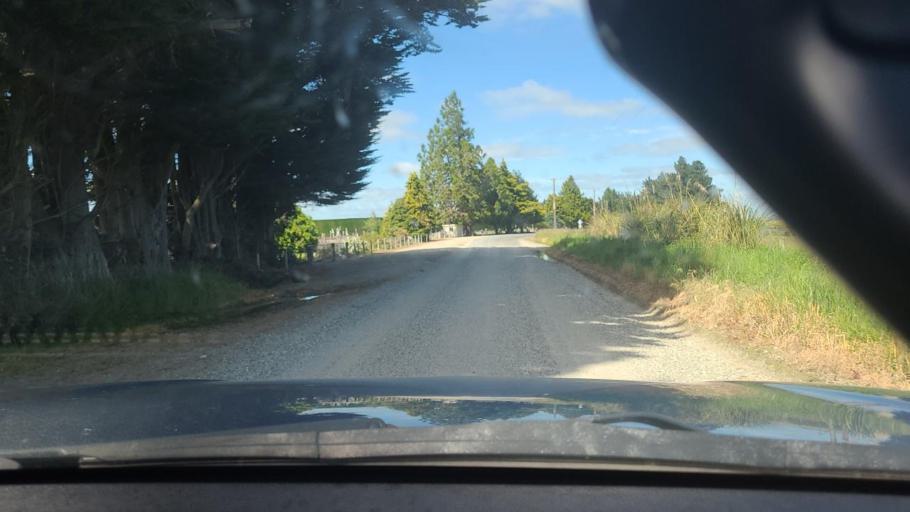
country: NZ
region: Southland
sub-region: Gore District
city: Gore
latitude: -46.3144
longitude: 168.8820
